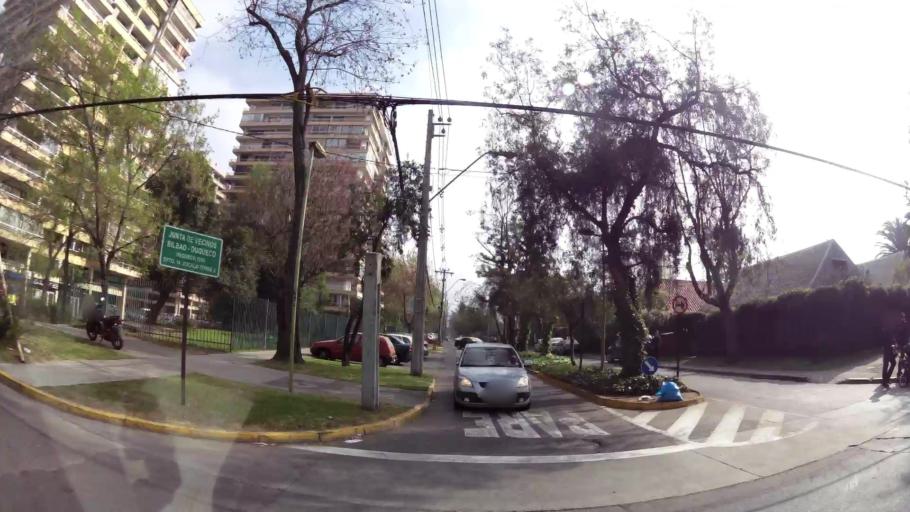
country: CL
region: Santiago Metropolitan
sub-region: Provincia de Santiago
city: Villa Presidente Frei, Nunoa, Santiago, Chile
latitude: -33.4296
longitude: -70.5476
